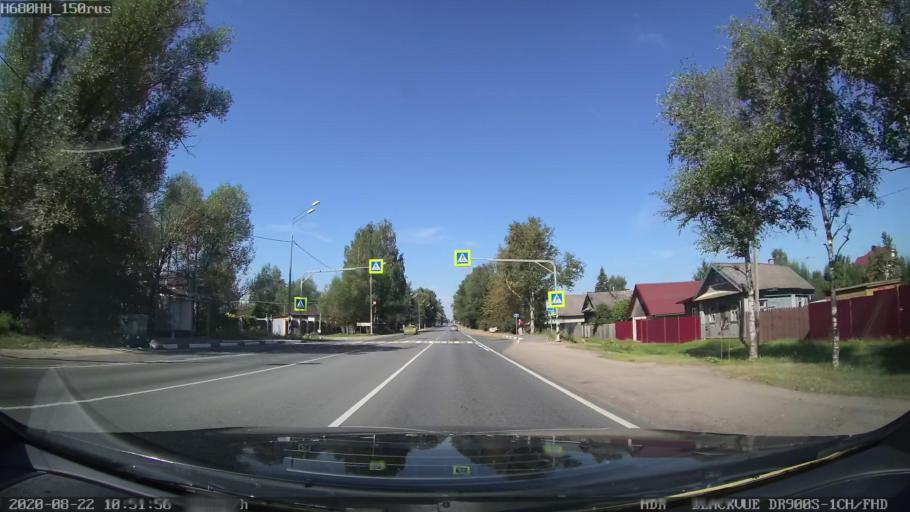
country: RU
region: Tverskaya
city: Emmaus
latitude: 56.7918
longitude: 36.0687
